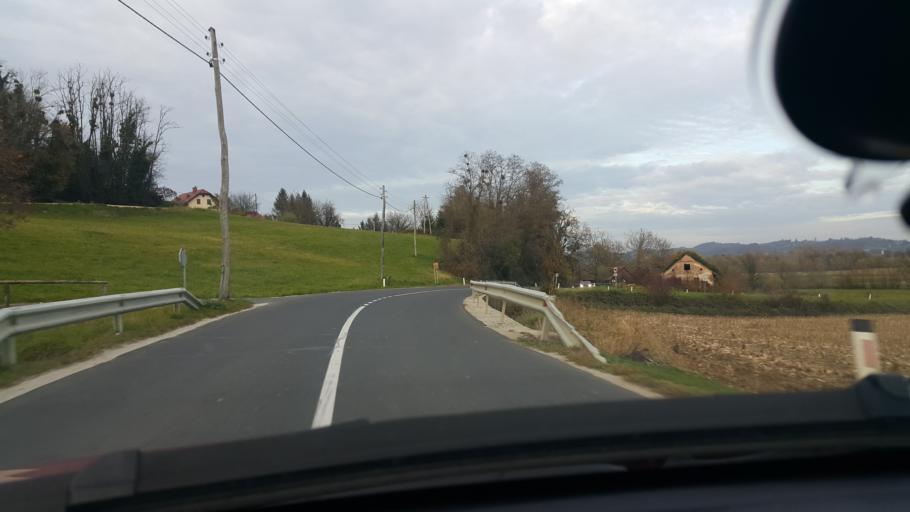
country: SI
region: Bistrica ob Sotli
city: Bistrica ob Sotli
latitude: 45.9740
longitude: 15.6963
